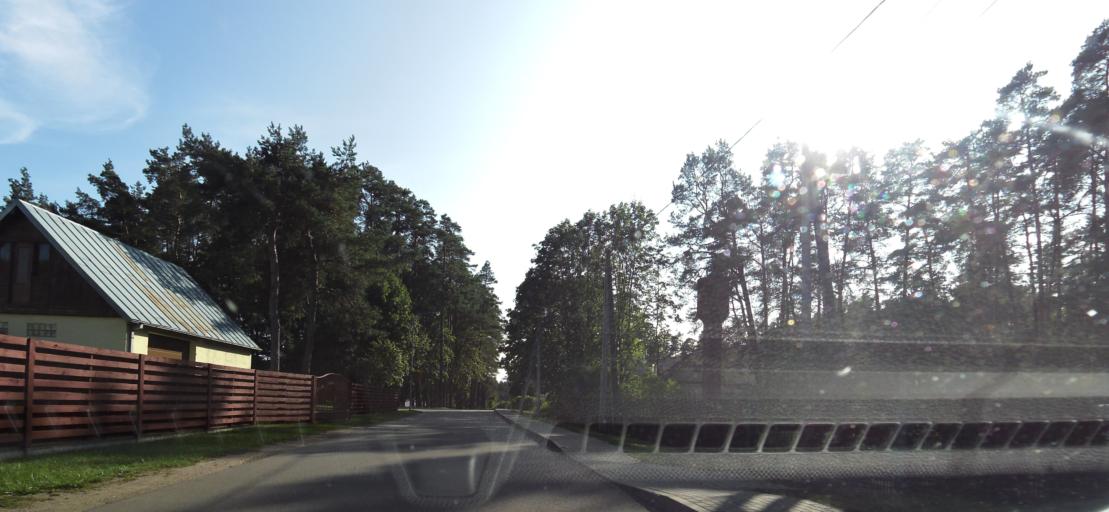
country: LT
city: Baltoji Voke
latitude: 54.5838
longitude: 25.2606
